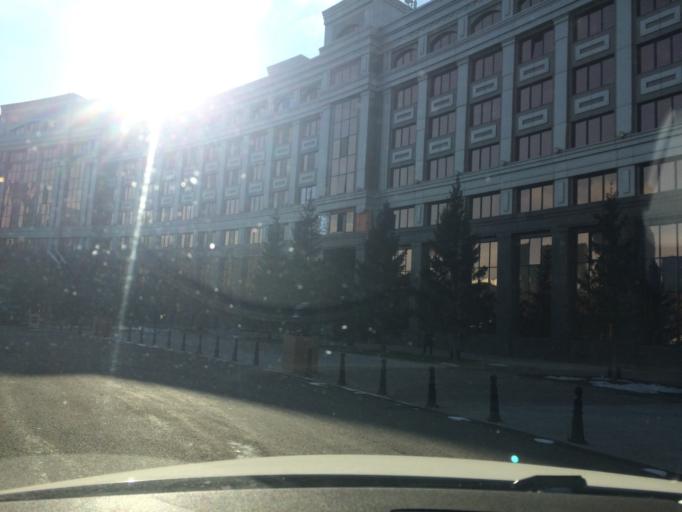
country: KZ
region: Astana Qalasy
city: Astana
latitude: 51.1307
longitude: 71.4126
